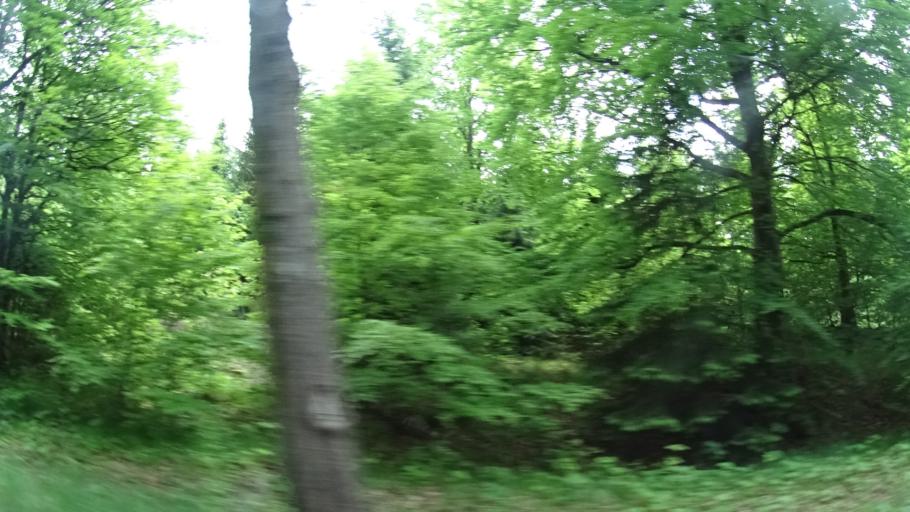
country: DE
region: Thuringia
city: Suhl
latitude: 50.6137
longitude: 10.7321
